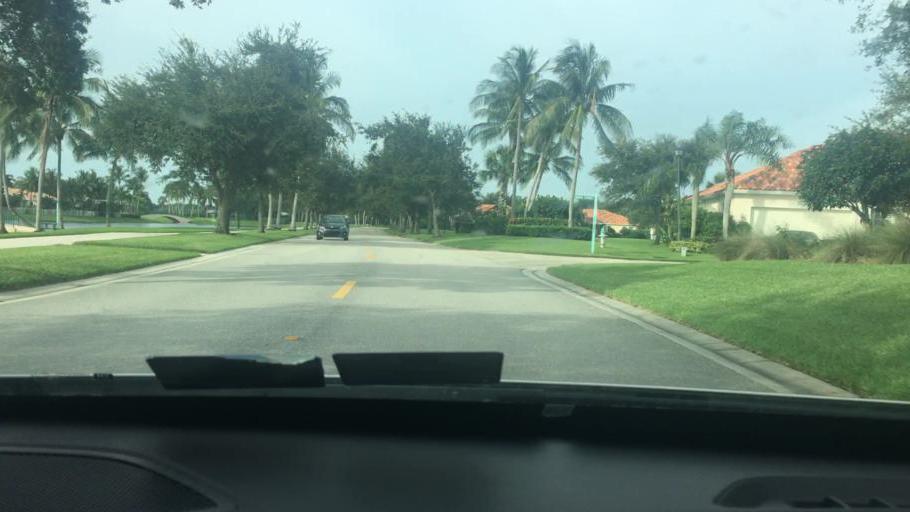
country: US
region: Florida
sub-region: Palm Beach County
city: Plantation Mobile Home Park
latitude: 26.7109
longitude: -80.1632
